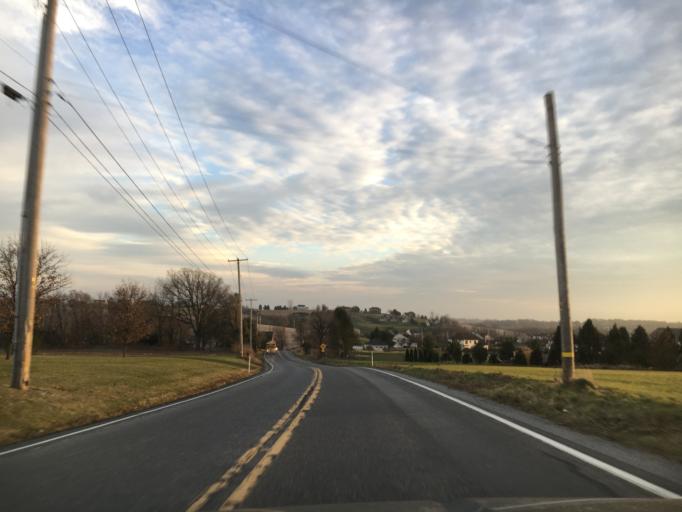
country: US
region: Pennsylvania
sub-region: Lehigh County
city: Schnecksville
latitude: 40.7078
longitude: -75.5973
